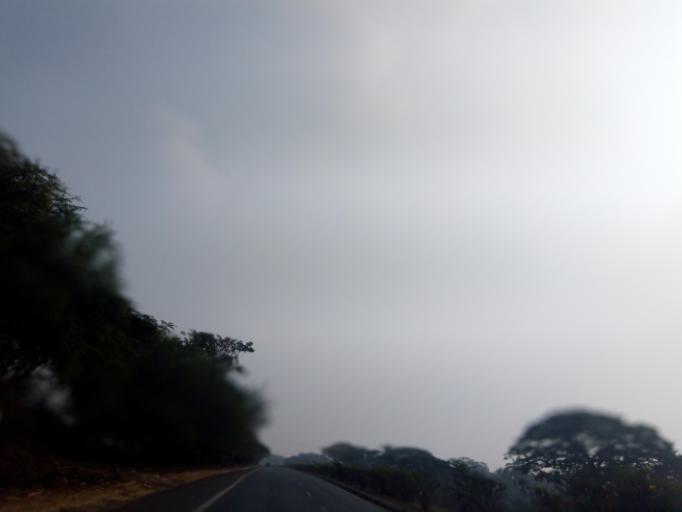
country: IN
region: Andhra Pradesh
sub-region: West Godavari
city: Tadepallegudem
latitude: 16.8186
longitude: 81.3926
